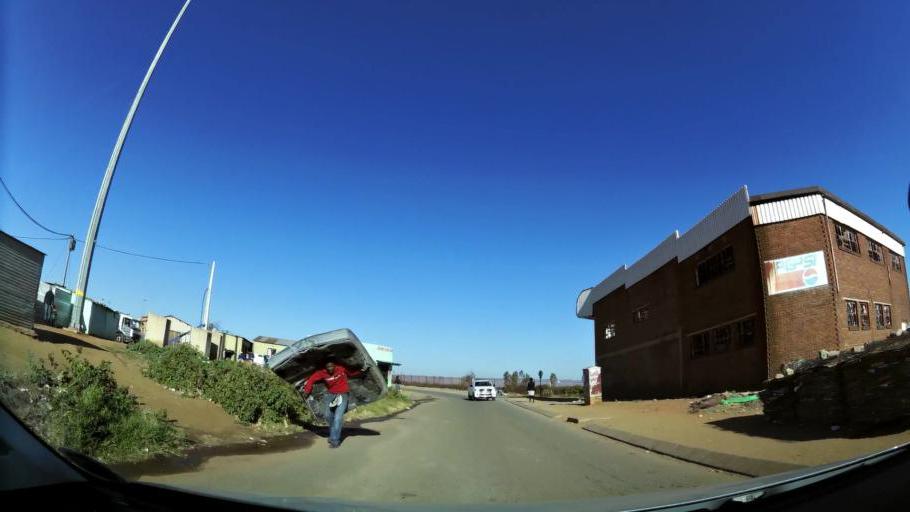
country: ZA
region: Gauteng
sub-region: Ekurhuleni Metropolitan Municipality
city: Tembisa
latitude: -26.0242
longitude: 28.2157
